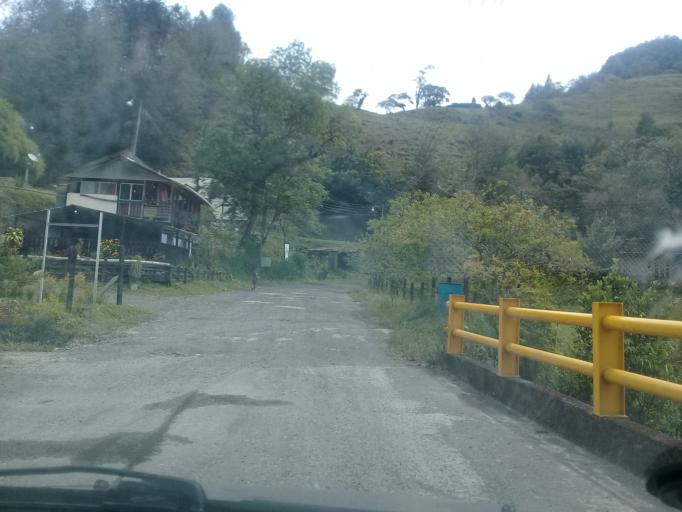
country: CO
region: Cundinamarca
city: Gachala
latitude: 4.7029
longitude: -73.4635
